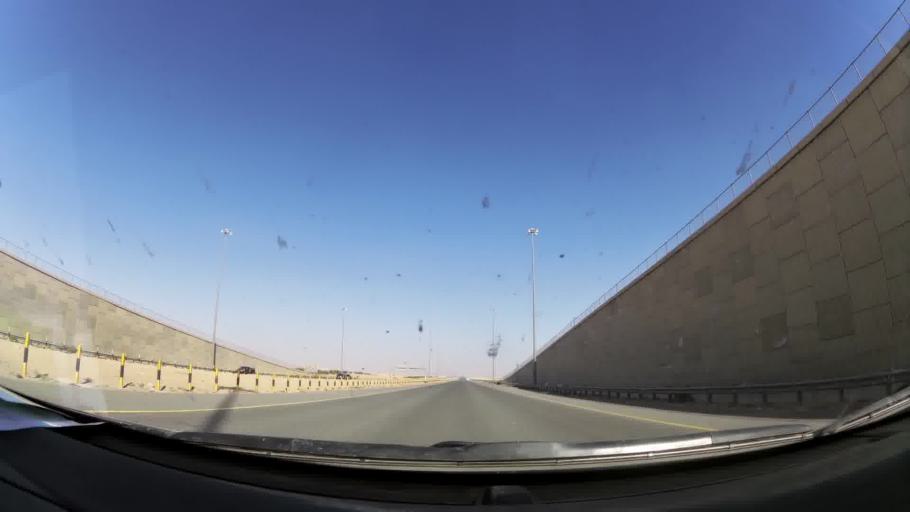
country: KW
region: Muhafazat al Jahra'
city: Al Jahra'
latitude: 29.4375
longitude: 47.7389
